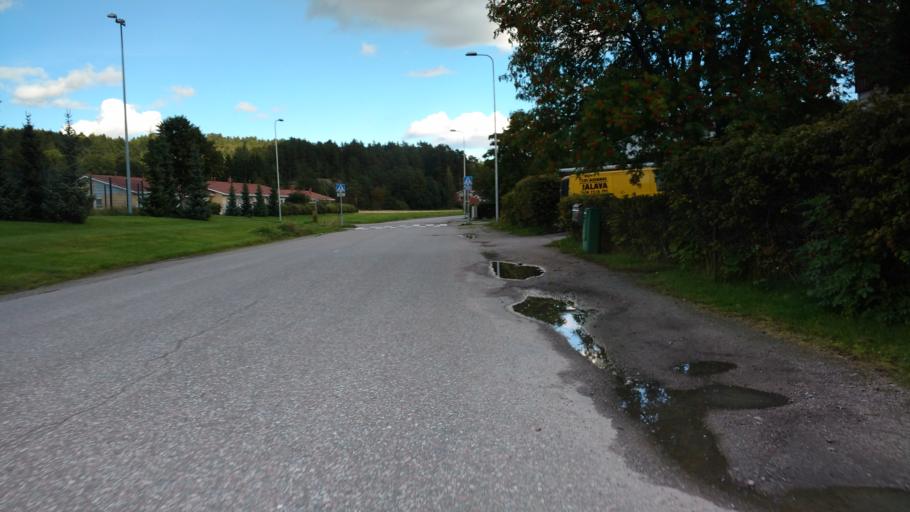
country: FI
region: Varsinais-Suomi
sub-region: Salo
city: Salo
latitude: 60.3809
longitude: 23.1593
